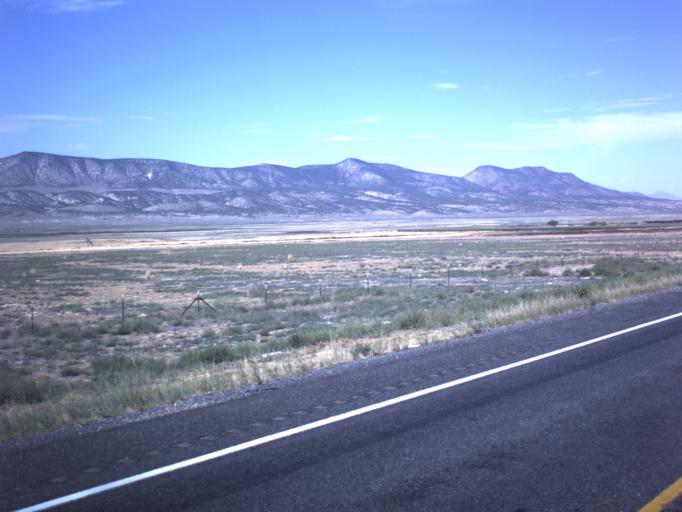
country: US
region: Utah
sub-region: Sanpete County
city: Gunnison
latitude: 39.2471
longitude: -111.8552
